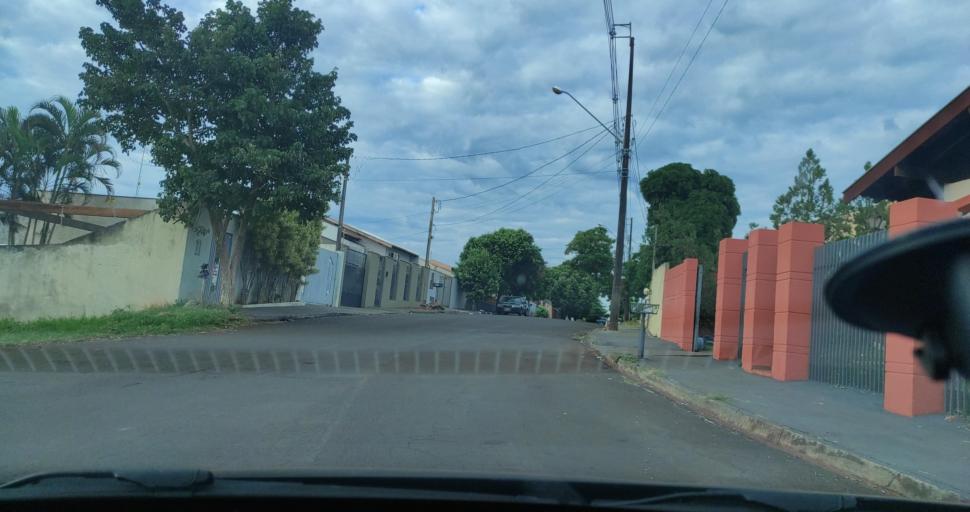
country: BR
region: Parana
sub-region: Ibipora
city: Ibipora
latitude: -23.2576
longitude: -51.0484
